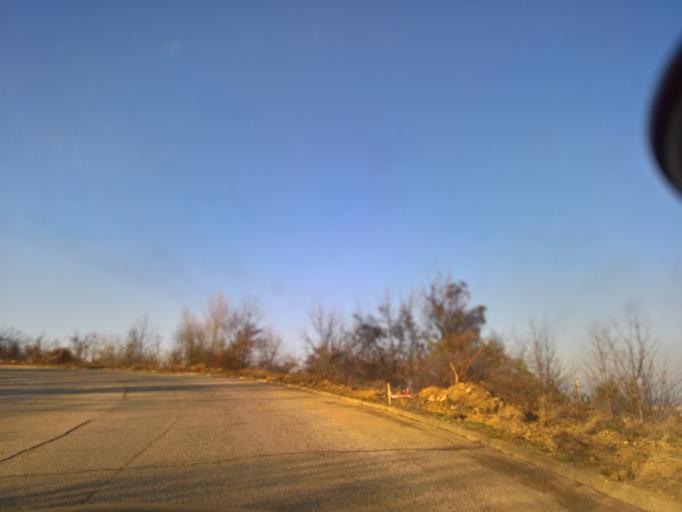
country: SK
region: Nitriansky
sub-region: Okres Nitra
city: Nitra
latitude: 48.3103
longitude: 18.0473
